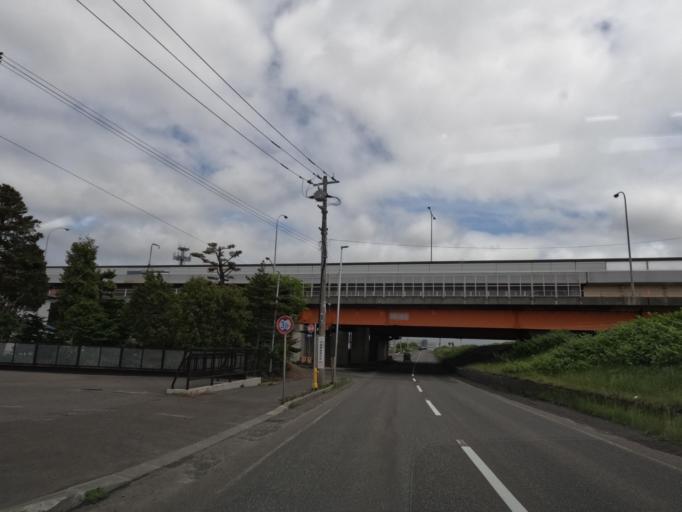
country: JP
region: Hokkaido
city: Sapporo
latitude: 43.0848
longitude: 141.4168
